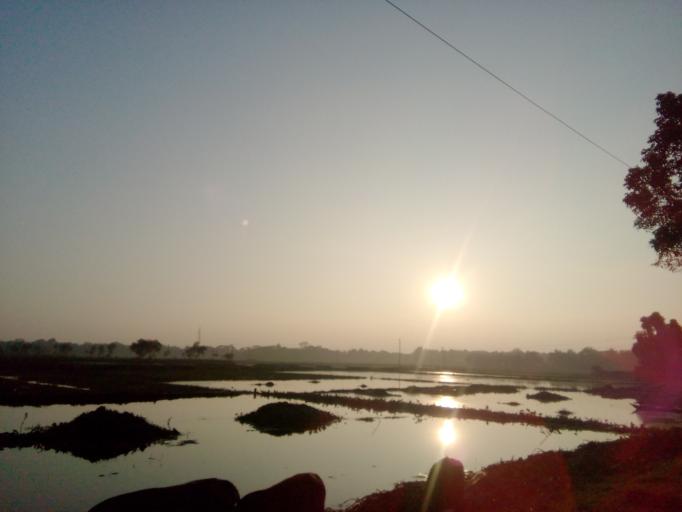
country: BD
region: Chittagong
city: Comilla
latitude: 23.4054
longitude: 91.1771
